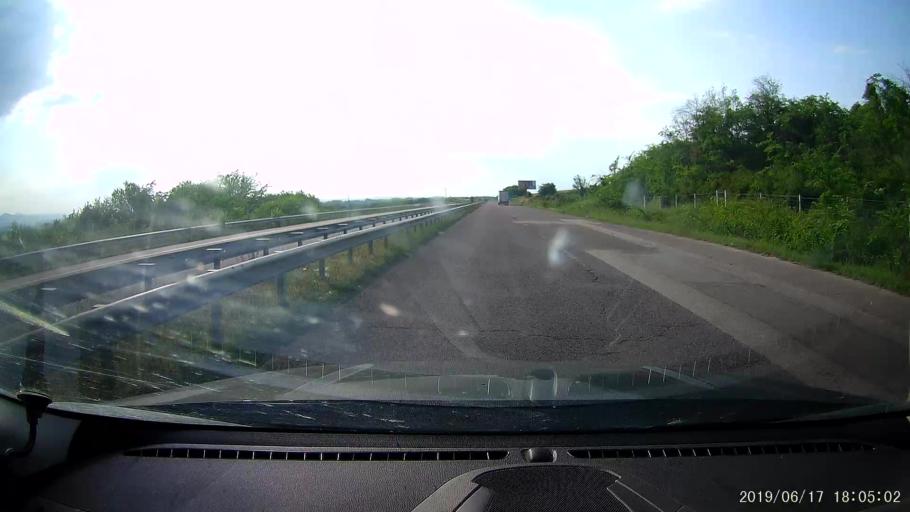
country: BG
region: Khaskovo
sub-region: Obshtina Svilengrad
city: Svilengrad
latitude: 41.7930
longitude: 26.1849
